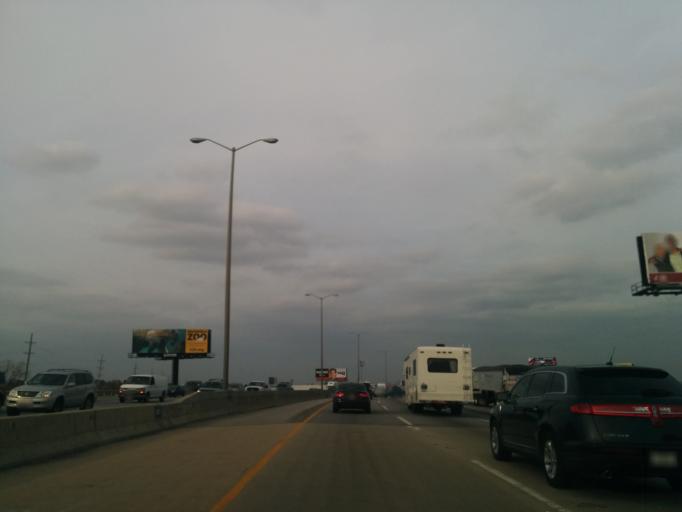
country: US
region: Illinois
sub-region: Cook County
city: Northlake
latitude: 41.9311
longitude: -87.9196
